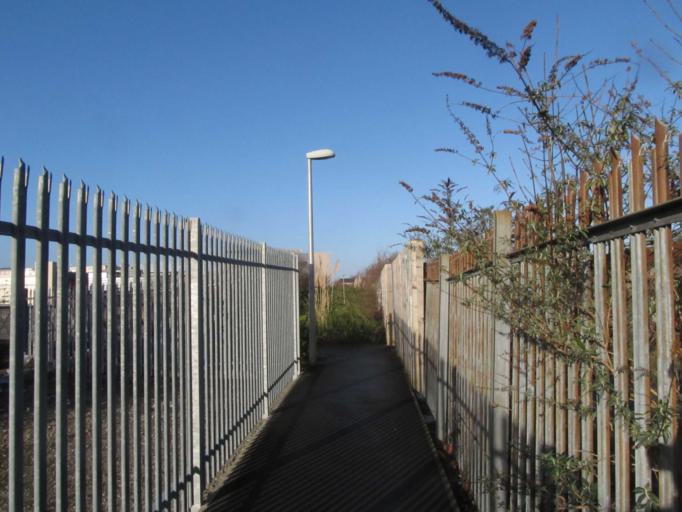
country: GB
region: England
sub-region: Nottingham
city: Nottingham
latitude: 52.9505
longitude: -1.1812
